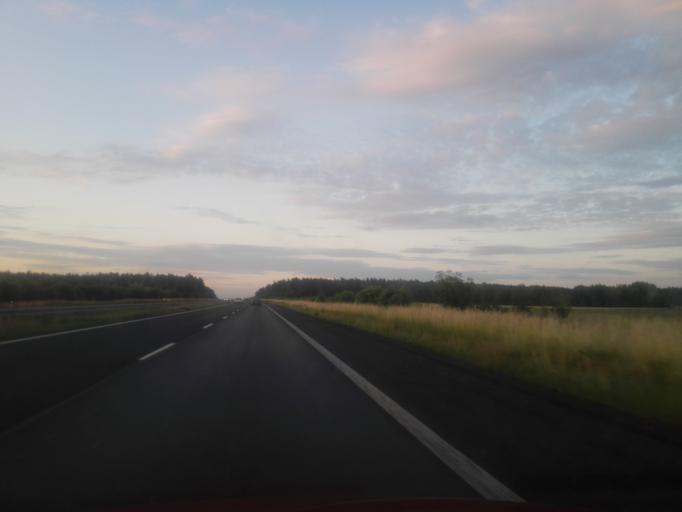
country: PL
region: Silesian Voivodeship
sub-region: Powiat czestochowski
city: Borowno
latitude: 50.9770
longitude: 19.2735
